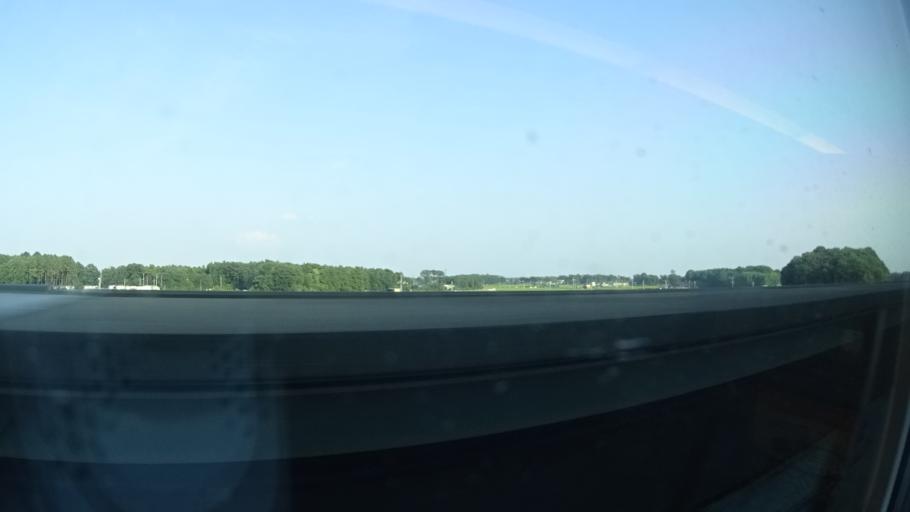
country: JP
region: Ibaraki
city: Koga
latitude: 36.2227
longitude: 139.7560
